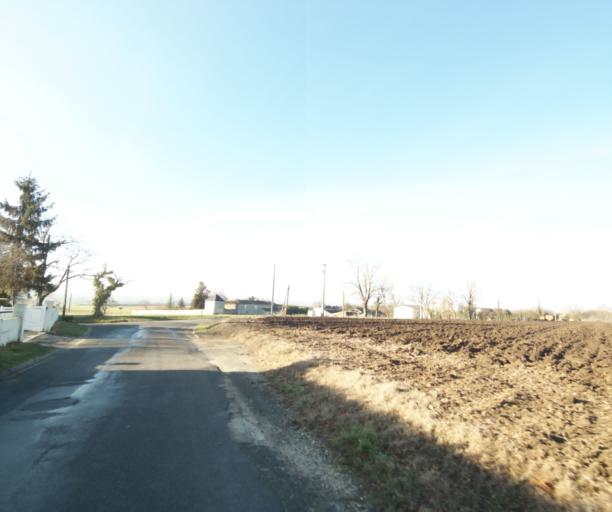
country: FR
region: Poitou-Charentes
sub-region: Departement de la Charente-Maritime
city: Cherac
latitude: 45.7050
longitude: -0.4478
